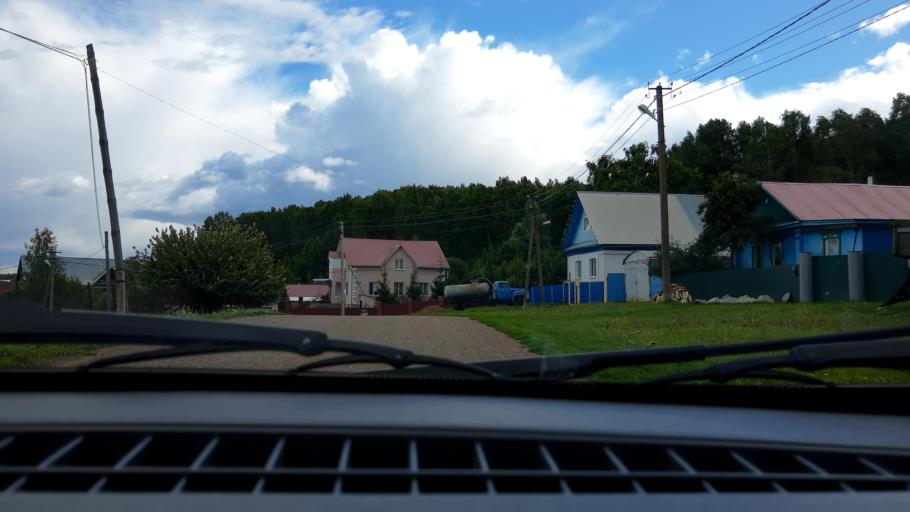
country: RU
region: Bashkortostan
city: Blagoveshchensk
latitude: 54.9438
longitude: 55.8745
